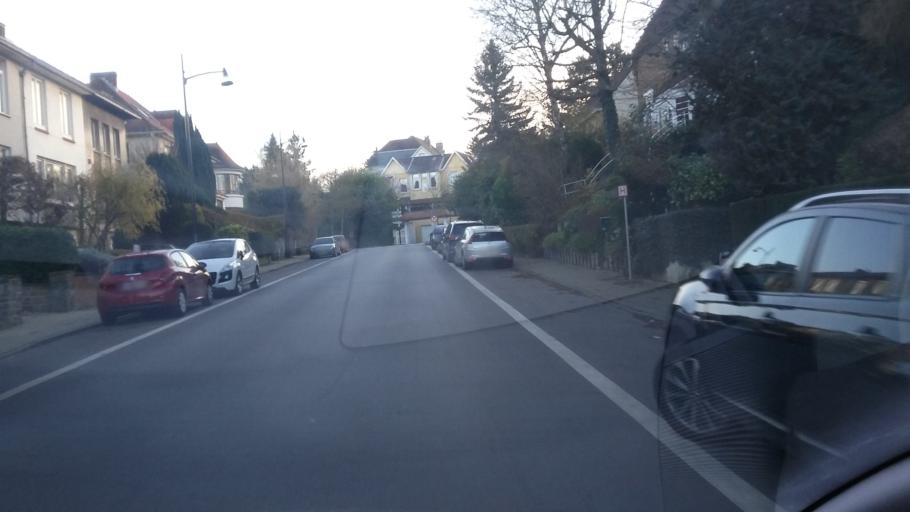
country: BE
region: Flanders
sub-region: Provincie Vlaams-Brabant
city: Hoeilaart
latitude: 50.8039
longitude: 4.4075
